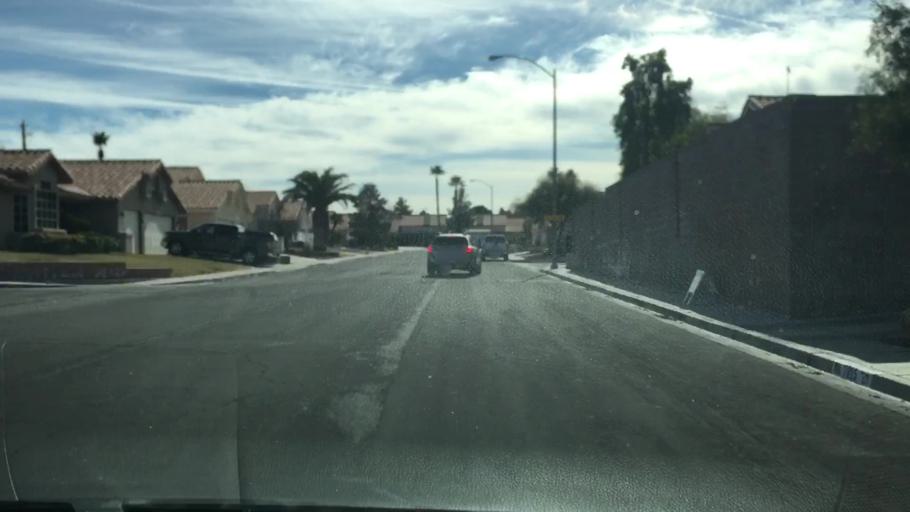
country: US
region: Nevada
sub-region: Clark County
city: Whitney
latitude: 36.0476
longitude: -115.1279
